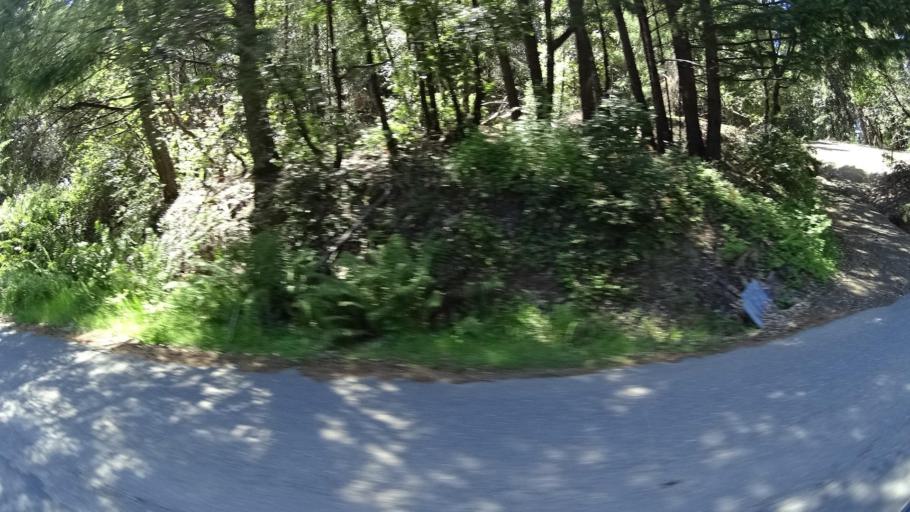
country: US
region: California
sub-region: Humboldt County
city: Rio Dell
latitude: 40.2615
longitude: -124.1025
